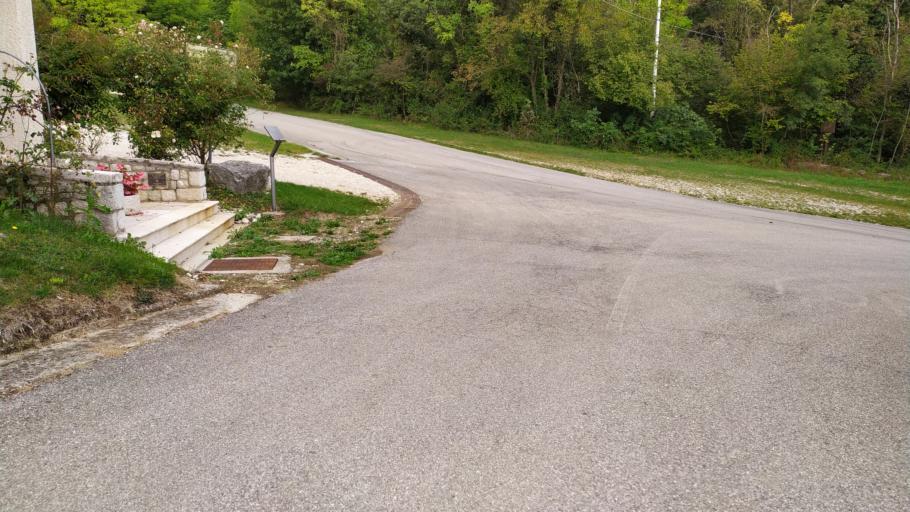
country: IT
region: Friuli Venezia Giulia
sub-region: Provincia di Pordenone
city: Marsure
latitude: 46.0890
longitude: 12.5731
